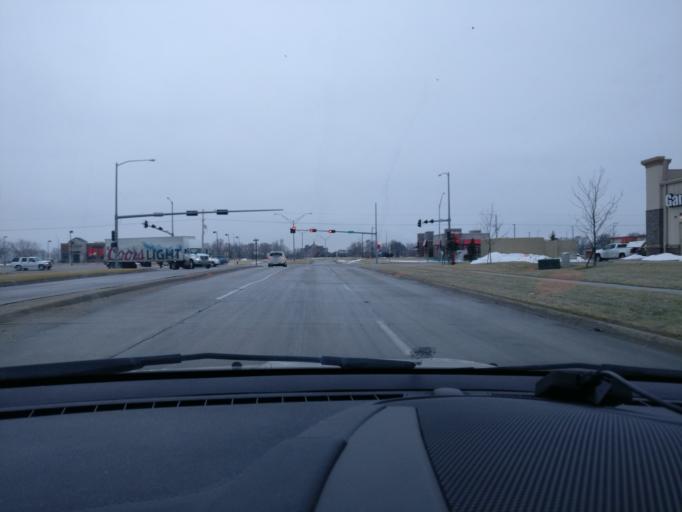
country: US
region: Nebraska
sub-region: Dodge County
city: Fremont
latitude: 41.4522
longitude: -96.4539
